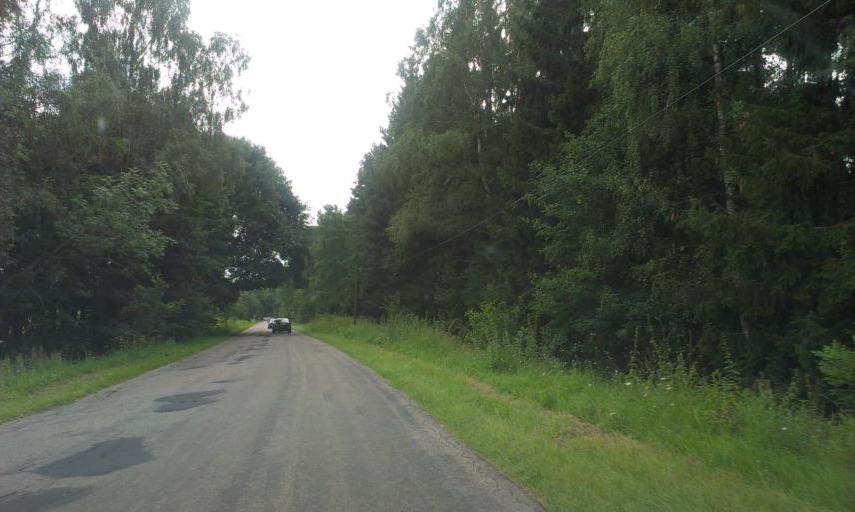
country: PL
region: West Pomeranian Voivodeship
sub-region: Powiat szczecinecki
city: Barwice
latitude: 53.6779
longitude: 16.3407
